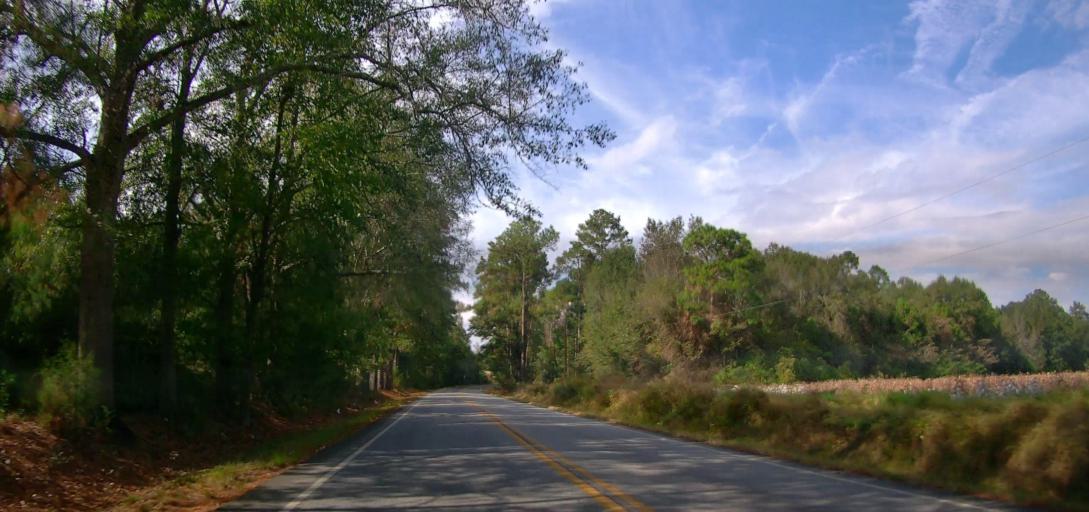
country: US
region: Georgia
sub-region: Thomas County
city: Thomasville
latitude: 30.9356
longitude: -84.0275
